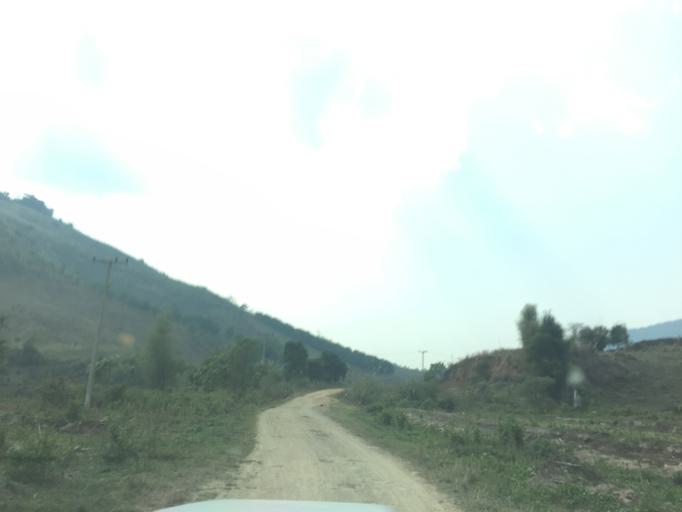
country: TH
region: Nan
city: Song Khwae
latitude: 19.7395
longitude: 100.7159
